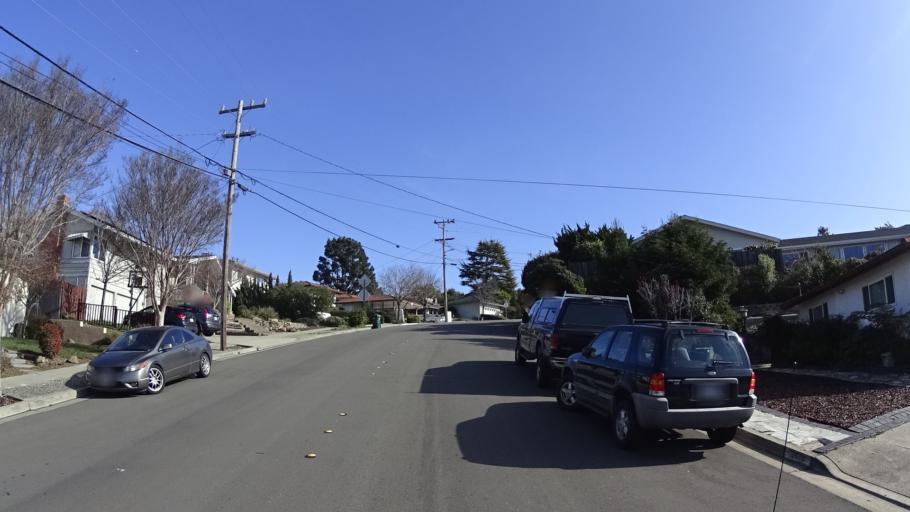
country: US
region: California
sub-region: Alameda County
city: Fairview
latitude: 37.6624
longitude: -122.0426
